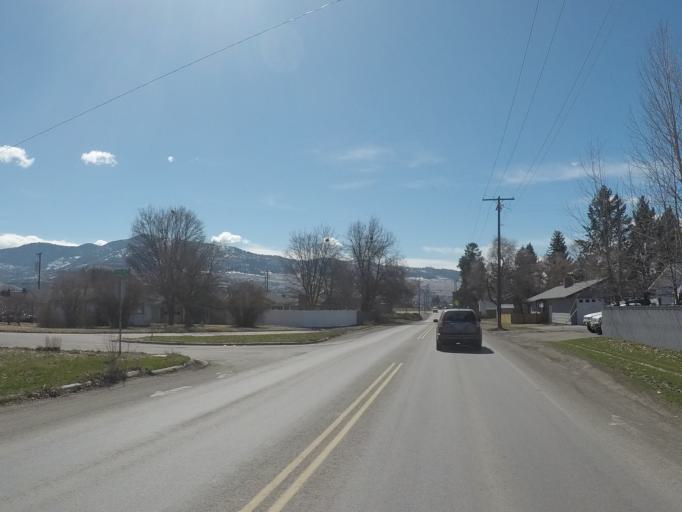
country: US
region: Montana
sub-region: Missoula County
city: Missoula
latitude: 46.8614
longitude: -114.0186
